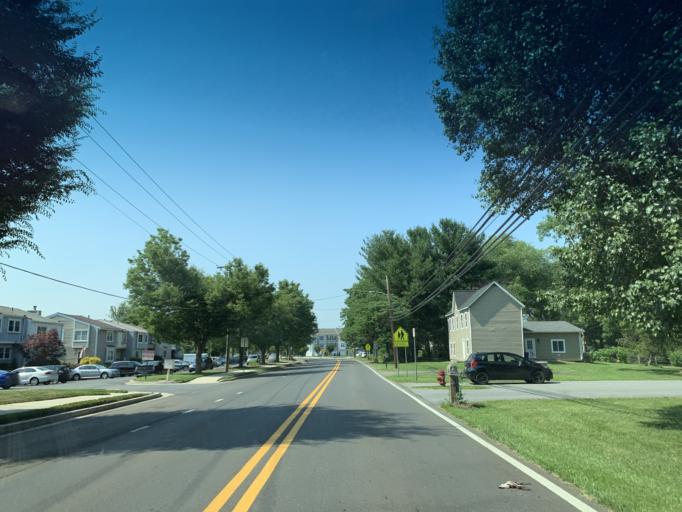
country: US
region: Maryland
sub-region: Montgomery County
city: Poolesville
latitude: 39.1409
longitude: -77.4073
